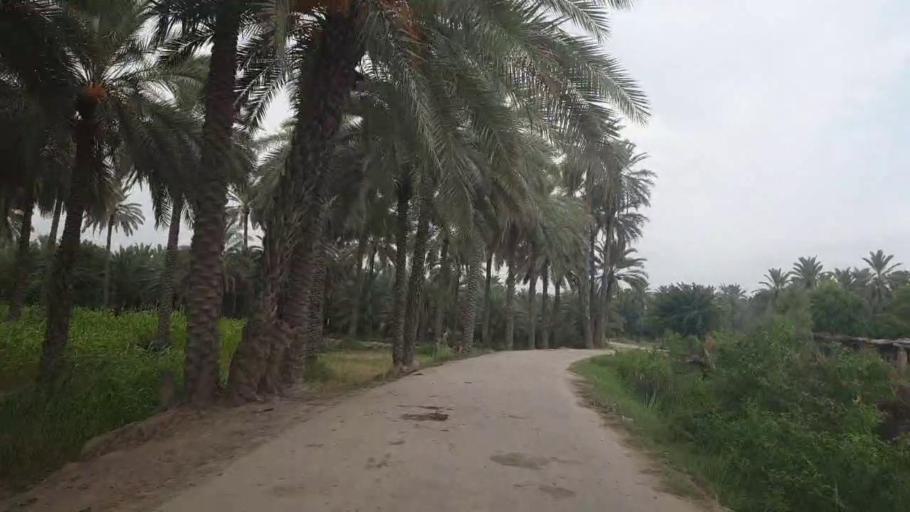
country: PK
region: Sindh
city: Khairpur
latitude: 27.5814
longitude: 68.7112
